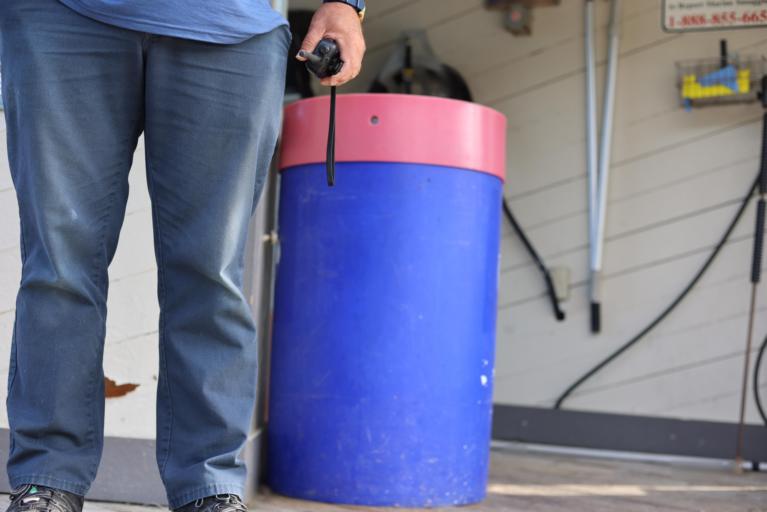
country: CA
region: British Columbia
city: Metchosin
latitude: 48.3473
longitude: -123.5718
